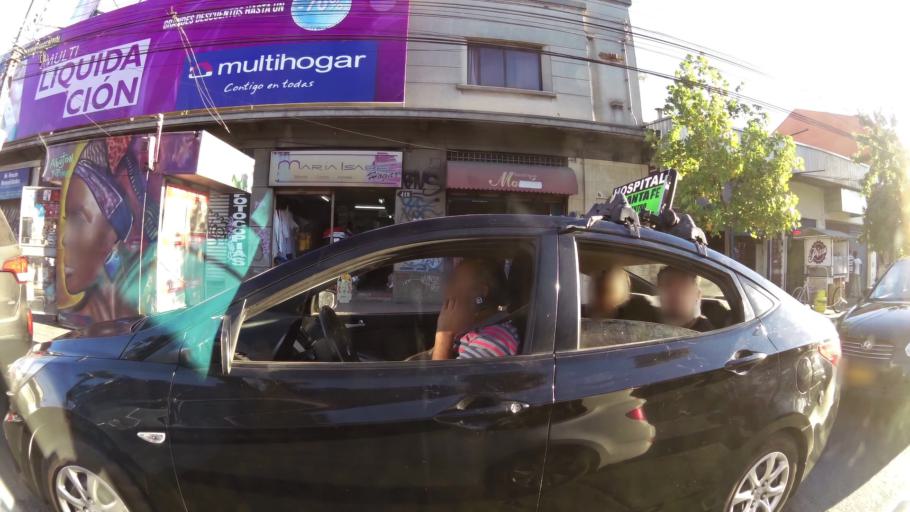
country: CL
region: Maule
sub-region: Provincia de Curico
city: Curico
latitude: -34.9813
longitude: -71.2410
